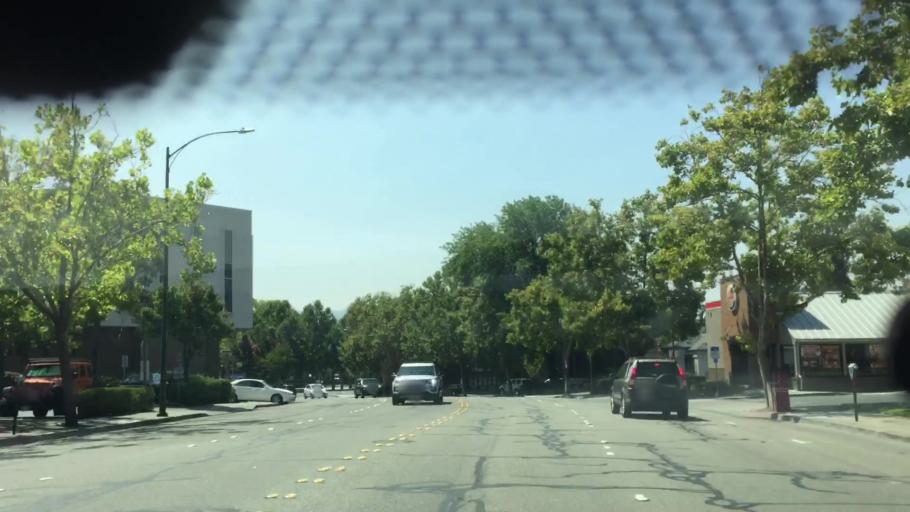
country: US
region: California
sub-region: Contra Costa County
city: Walnut Creek
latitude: 37.9037
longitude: -122.0612
